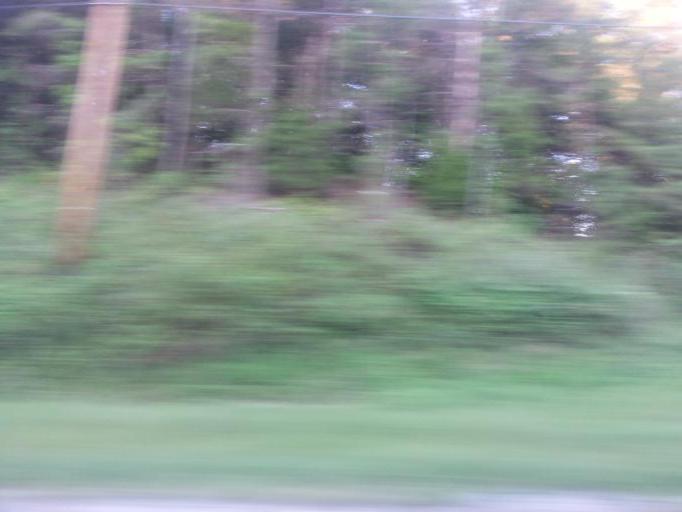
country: US
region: Tennessee
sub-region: Roane County
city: Midtown
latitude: 35.8426
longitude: -84.5425
